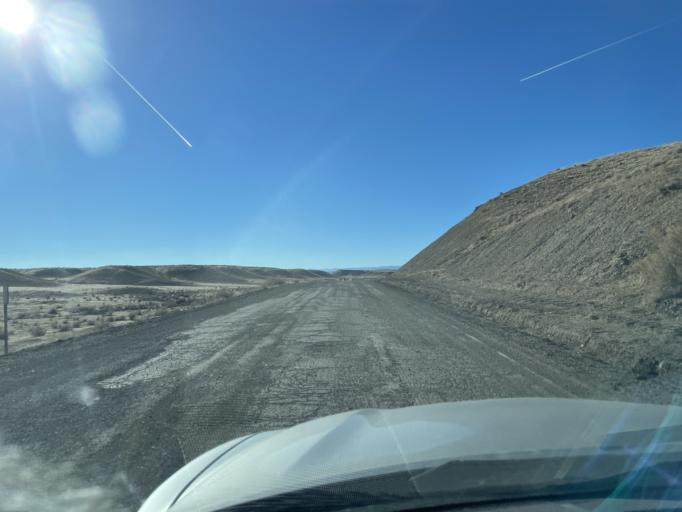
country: US
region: Colorado
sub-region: Mesa County
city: Loma
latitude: 39.2059
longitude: -109.0933
